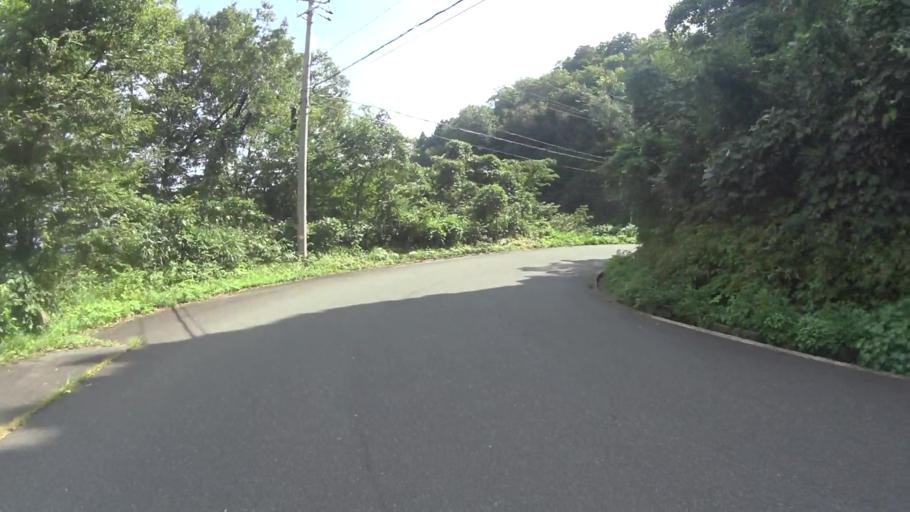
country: JP
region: Kyoto
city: Miyazu
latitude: 35.7168
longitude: 135.1941
